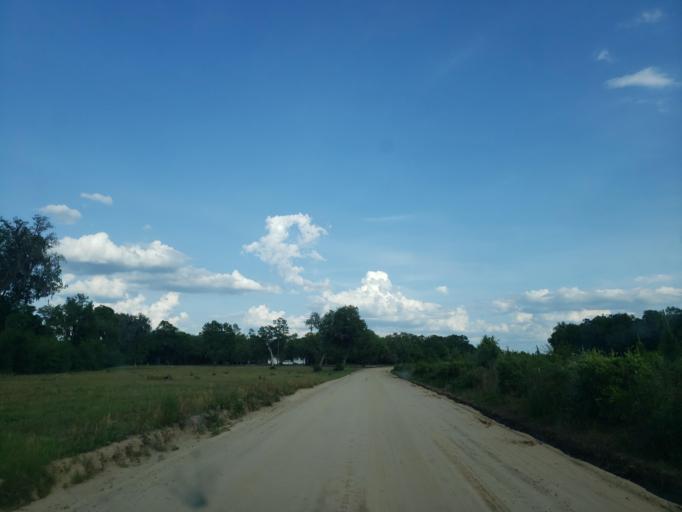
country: US
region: Georgia
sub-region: Echols County
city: Statenville
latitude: 30.6242
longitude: -83.1902
